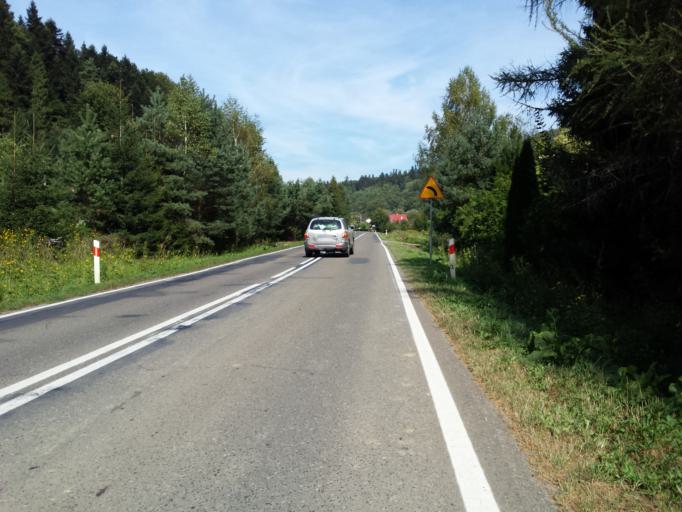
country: PL
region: Subcarpathian Voivodeship
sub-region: Powiat leski
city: Lesko
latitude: 49.4452
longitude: 22.3482
